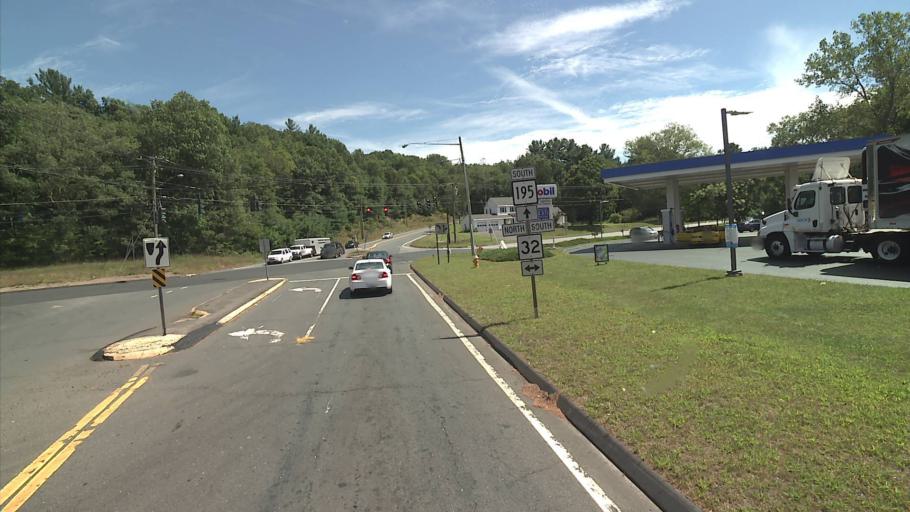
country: US
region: Connecticut
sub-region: Tolland County
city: Storrs
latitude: 41.8352
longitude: -72.3072
